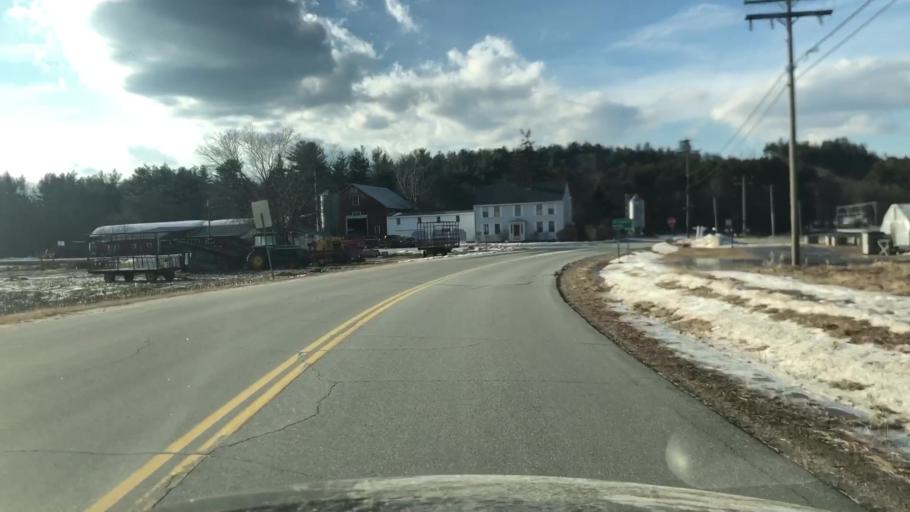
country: US
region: New Hampshire
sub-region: Hillsborough County
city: Wilton
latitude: 42.8523
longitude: -71.6969
